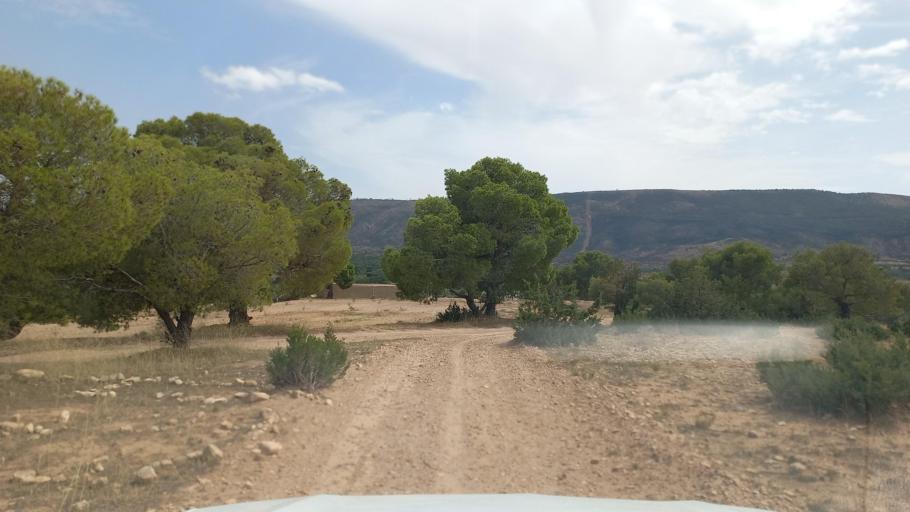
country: TN
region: Al Qasrayn
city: Kasserine
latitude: 35.3697
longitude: 8.8932
